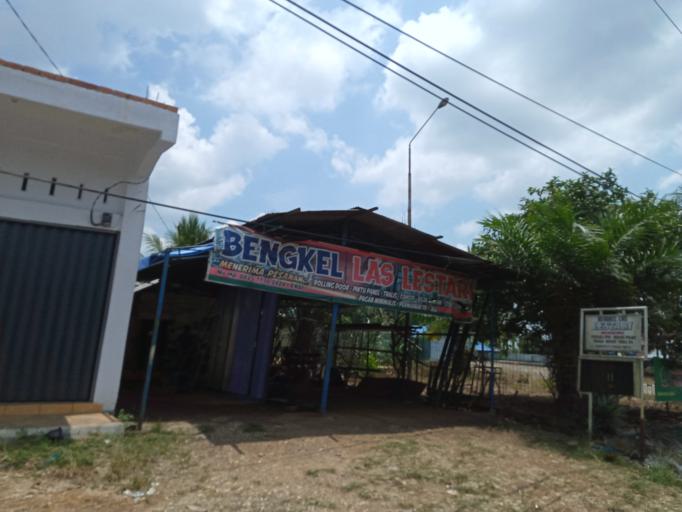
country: ID
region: Jambi
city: Bangko
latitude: -2.0863
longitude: 102.2585
